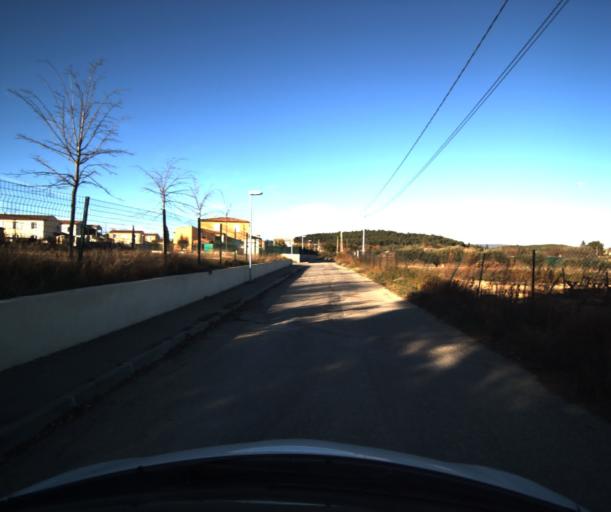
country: FR
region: Provence-Alpes-Cote d'Azur
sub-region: Departement du Vaucluse
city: Pertuis
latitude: 43.7061
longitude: 5.4997
